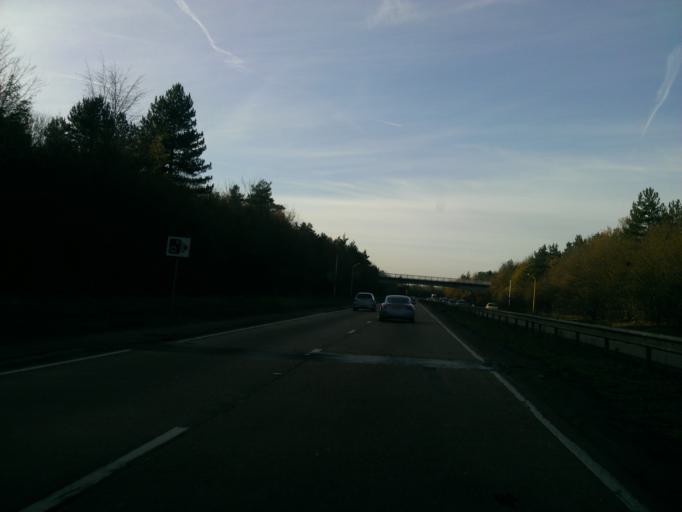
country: GB
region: England
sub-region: Essex
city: Kelvedon
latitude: 51.8327
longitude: 0.7136
